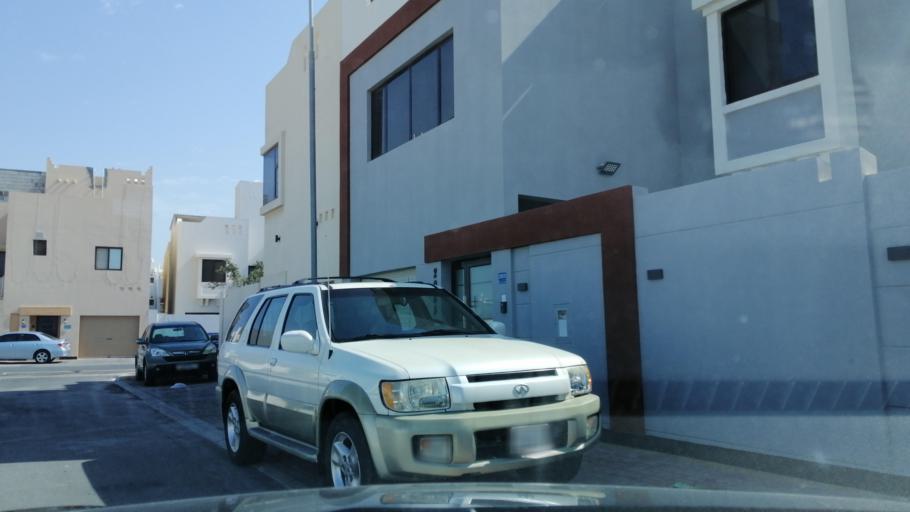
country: BH
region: Muharraq
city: Al Muharraq
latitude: 26.2485
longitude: 50.6293
